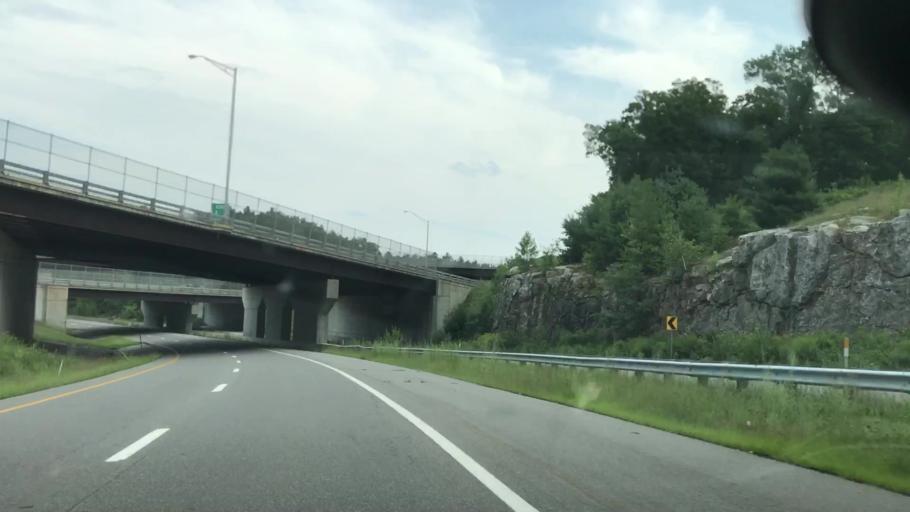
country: US
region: New Hampshire
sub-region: Hillsborough County
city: Hudson
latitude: 42.7238
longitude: -71.4513
